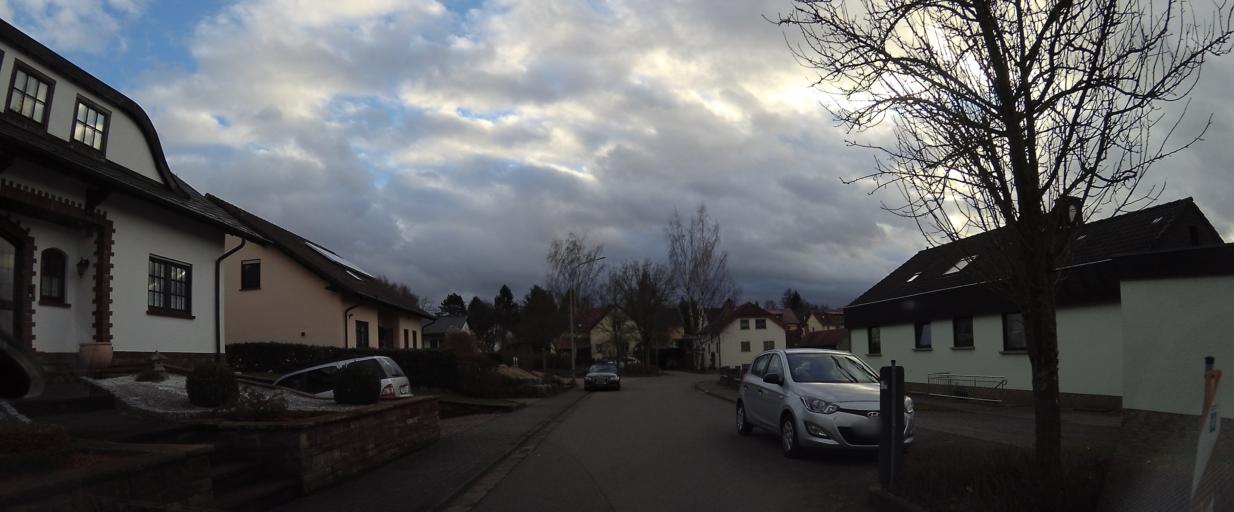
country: DE
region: Saarland
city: Schiffweiler
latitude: 49.3750
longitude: 7.0948
